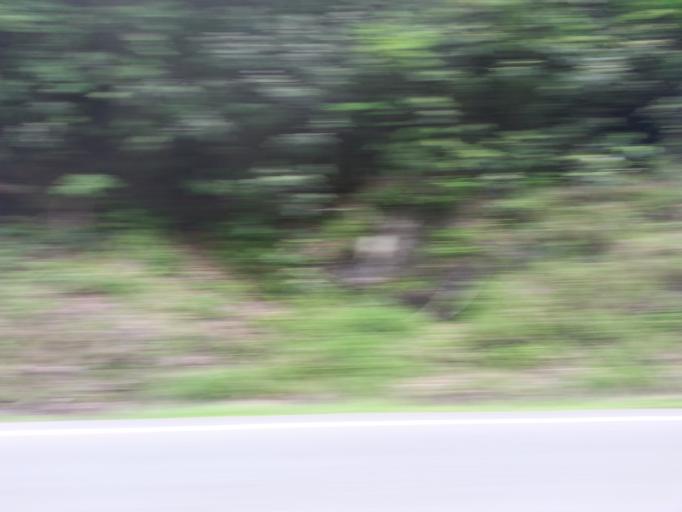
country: US
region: North Carolina
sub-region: Cherokee County
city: Andrews
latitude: 35.2286
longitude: -83.7361
